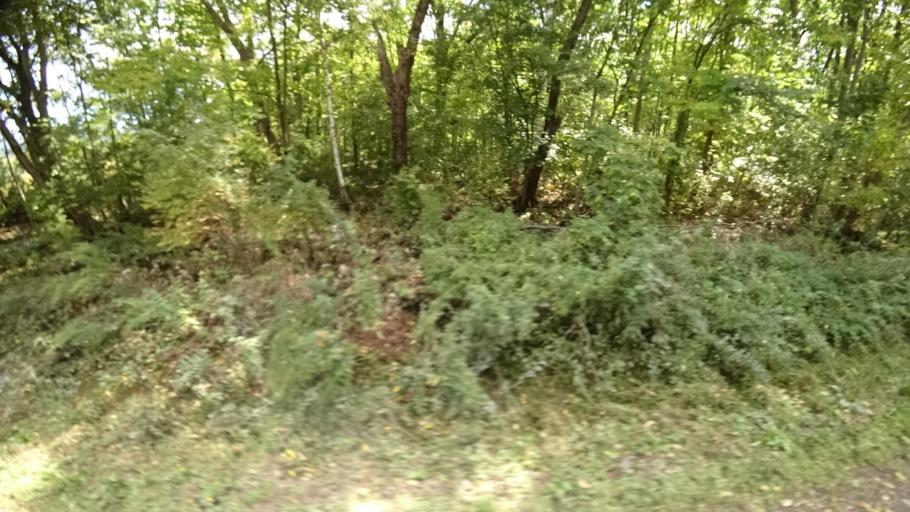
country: RU
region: Primorskiy
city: Yakovlevka
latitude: 44.6605
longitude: 133.7492
